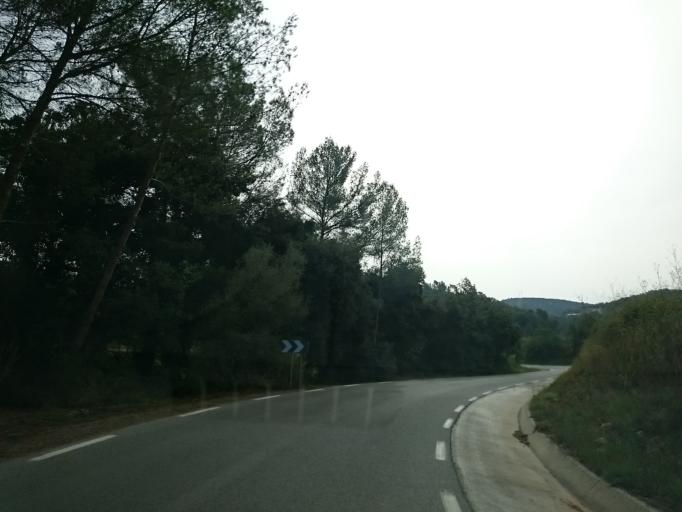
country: ES
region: Catalonia
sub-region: Provincia de Barcelona
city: Olivella
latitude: 41.3128
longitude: 1.8051
